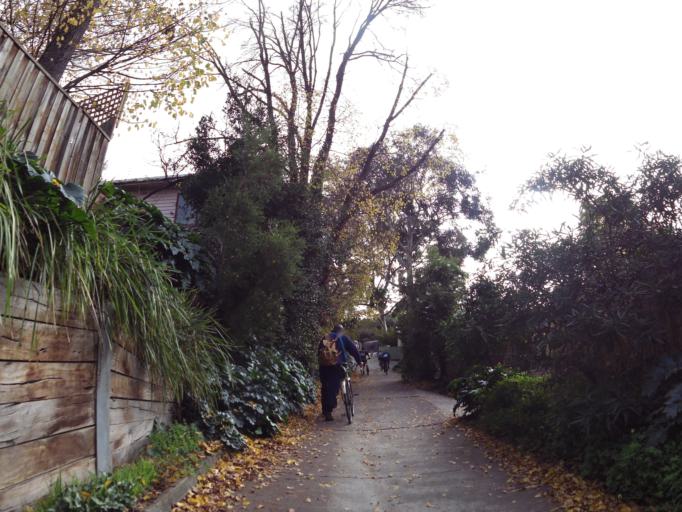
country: AU
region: Victoria
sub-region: Yarra
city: Richmond
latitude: -37.8082
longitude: 145.0132
